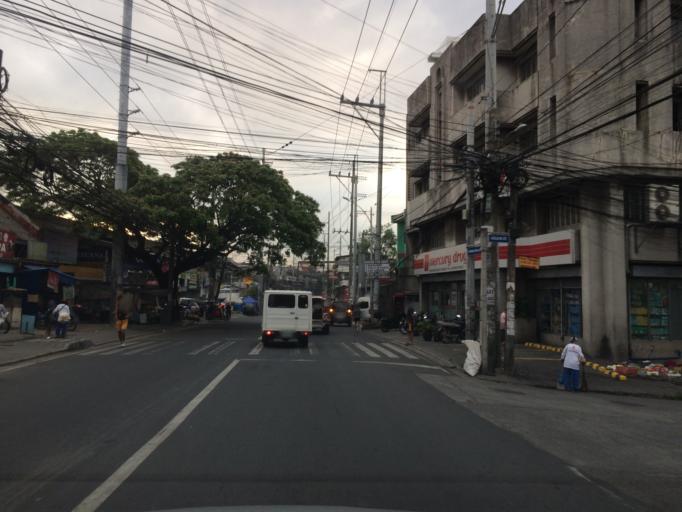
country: PH
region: Calabarzon
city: Bagong Pagasa
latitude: 14.6763
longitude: 121.0427
